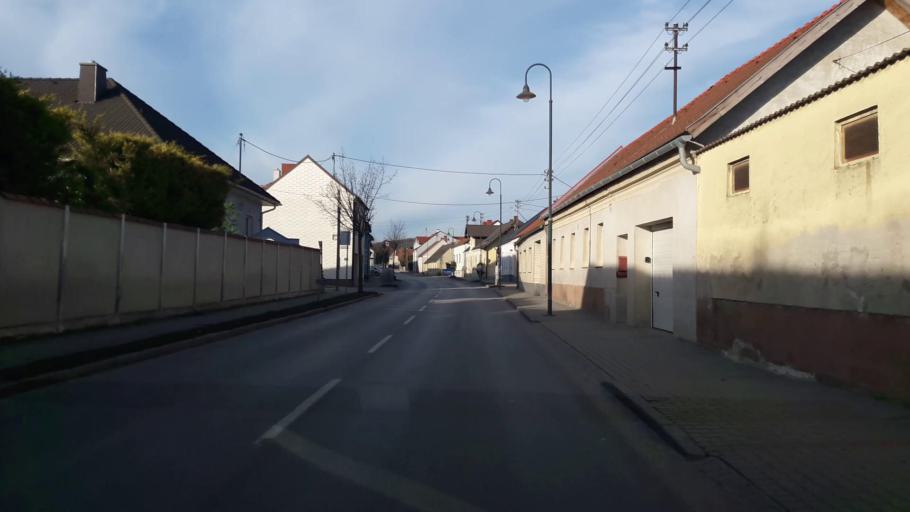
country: AT
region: Lower Austria
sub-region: Politischer Bezirk Ganserndorf
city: Gross-Schweinbarth
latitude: 48.4174
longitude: 16.6324
